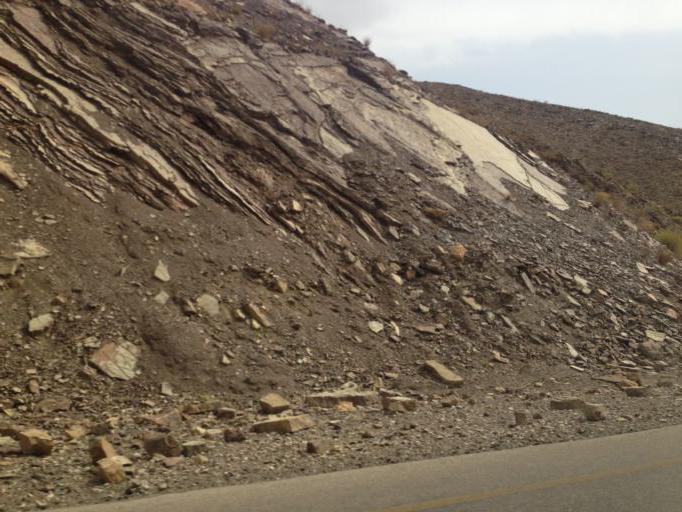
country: OM
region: Ash Sharqiyah
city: Badiyah
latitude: 22.5329
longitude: 58.9588
